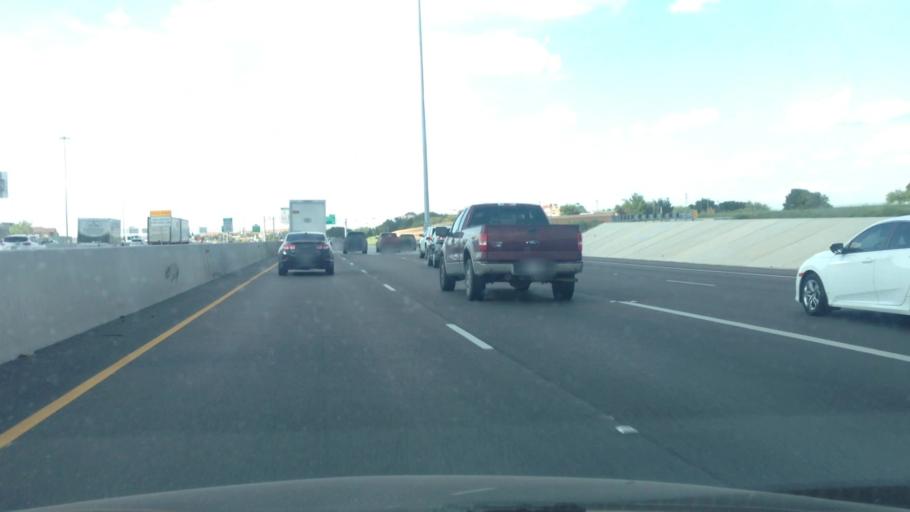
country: US
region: Texas
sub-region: Tarrant County
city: Blue Mound
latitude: 32.8491
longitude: -97.3118
